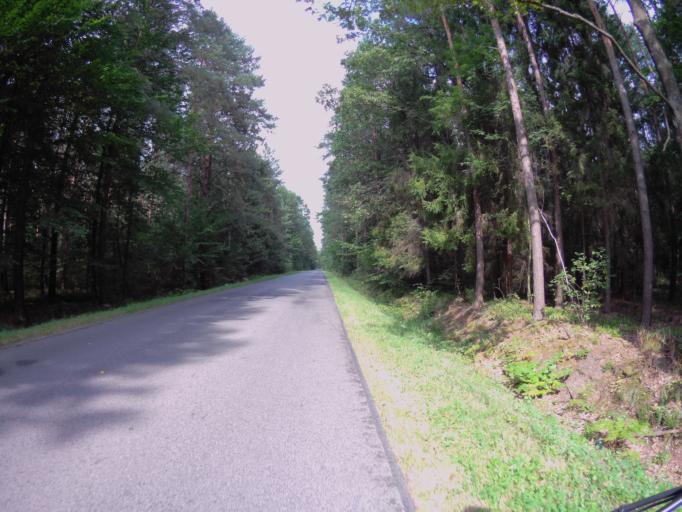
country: PL
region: Subcarpathian Voivodeship
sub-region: Powiat lezajski
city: Brzoza Krolewska
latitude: 50.2572
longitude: 22.3666
